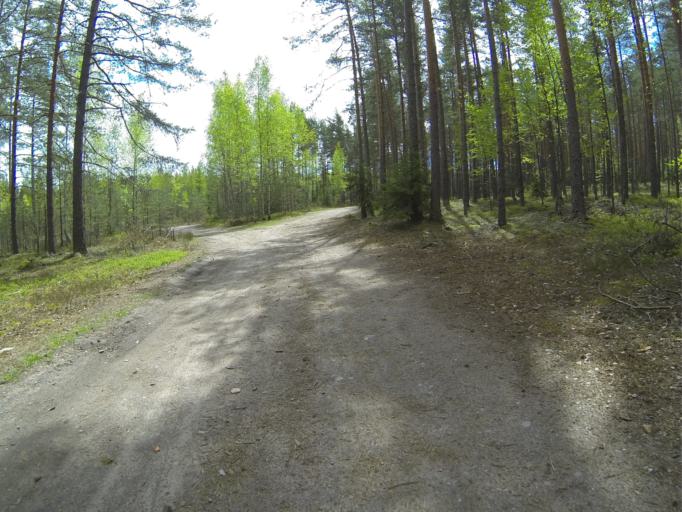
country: FI
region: Varsinais-Suomi
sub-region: Salo
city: Salo
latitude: 60.3122
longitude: 23.0835
